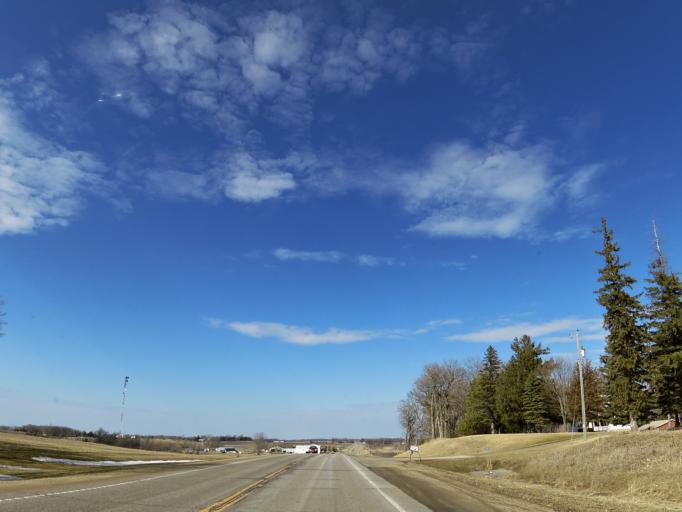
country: US
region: Minnesota
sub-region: Waseca County
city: Waseca
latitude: 44.1350
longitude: -93.5071
